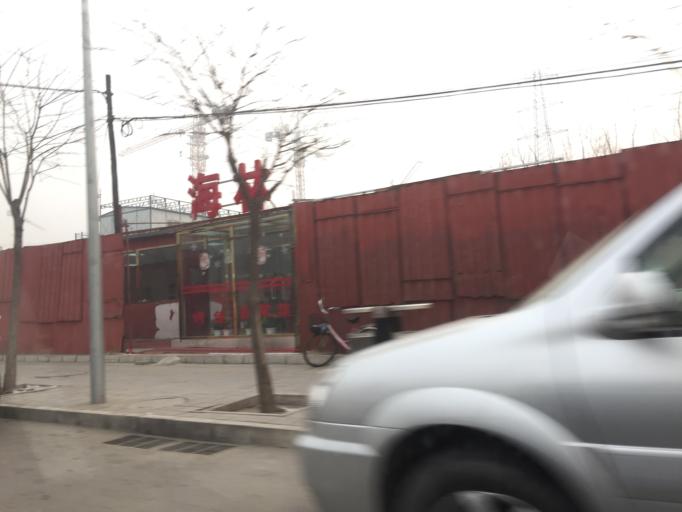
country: CN
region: Beijing
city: Qinghe
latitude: 40.0136
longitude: 116.3327
